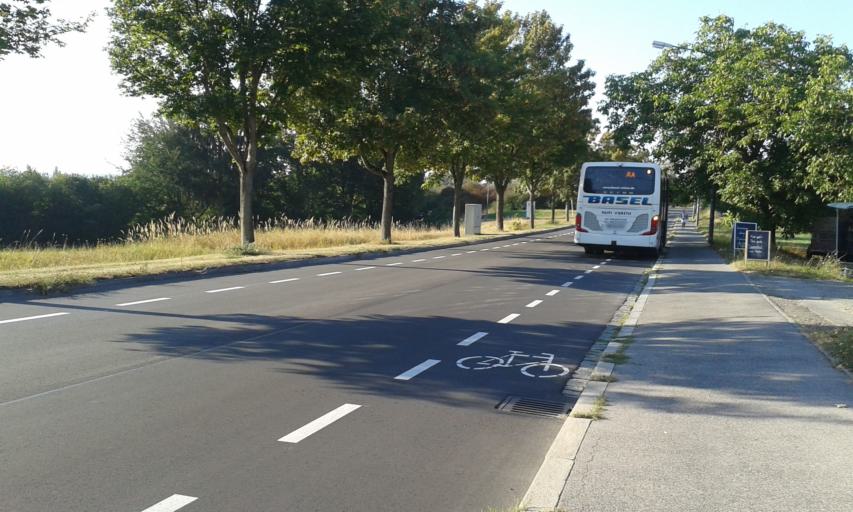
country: DE
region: Bavaria
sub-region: Upper Franconia
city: Bamberg
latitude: 49.8750
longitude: 10.8831
